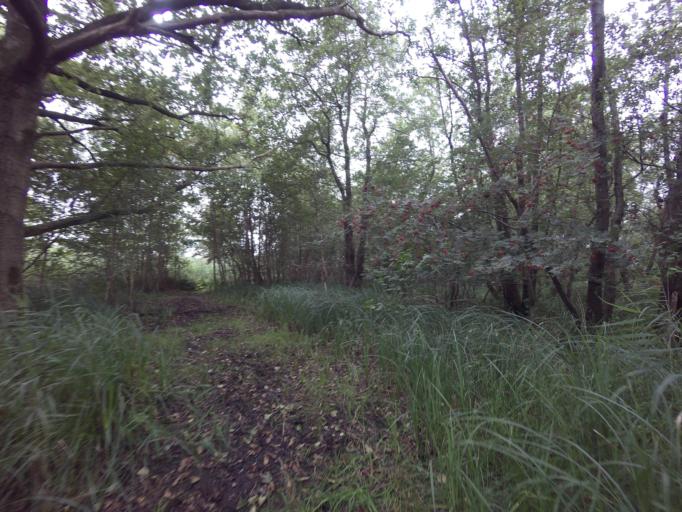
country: NL
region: Overijssel
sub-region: Gemeente Steenwijkerland
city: Sint Jansklooster
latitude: 52.7193
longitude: 6.0261
